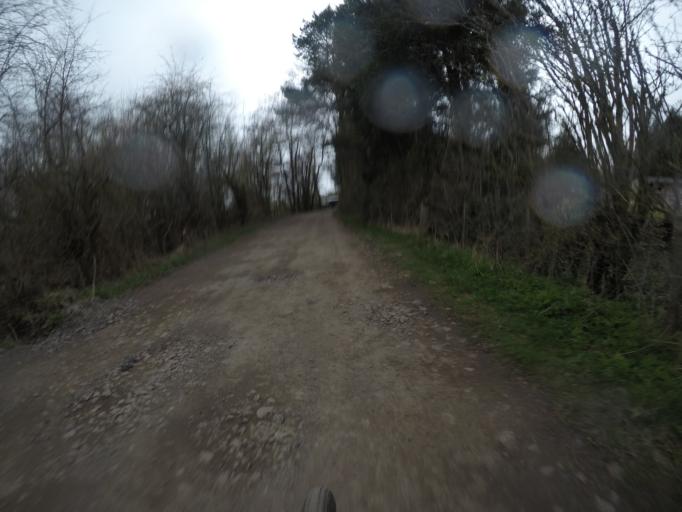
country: GB
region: Scotland
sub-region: East Ayrshire
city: Galston
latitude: 55.6065
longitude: -4.4084
